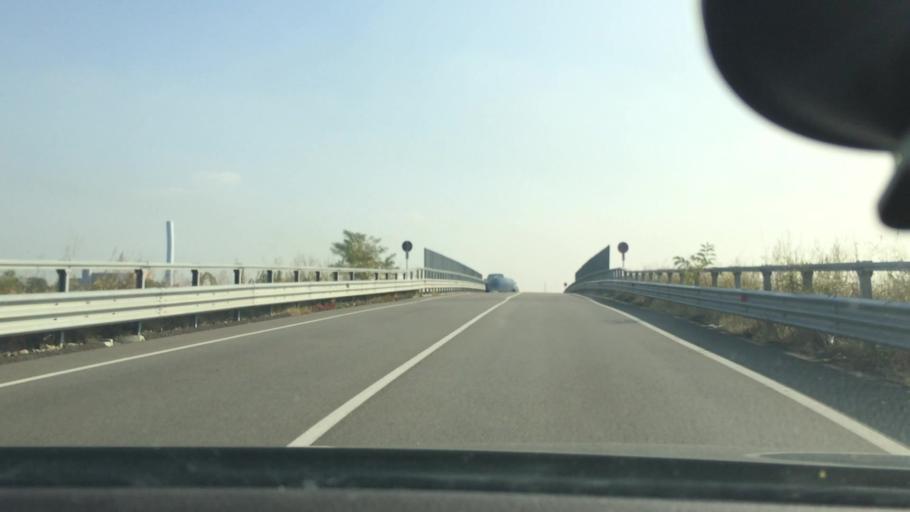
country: IT
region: Lombardy
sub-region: Citta metropolitana di Milano
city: Rho
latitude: 45.5127
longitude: 9.0567
